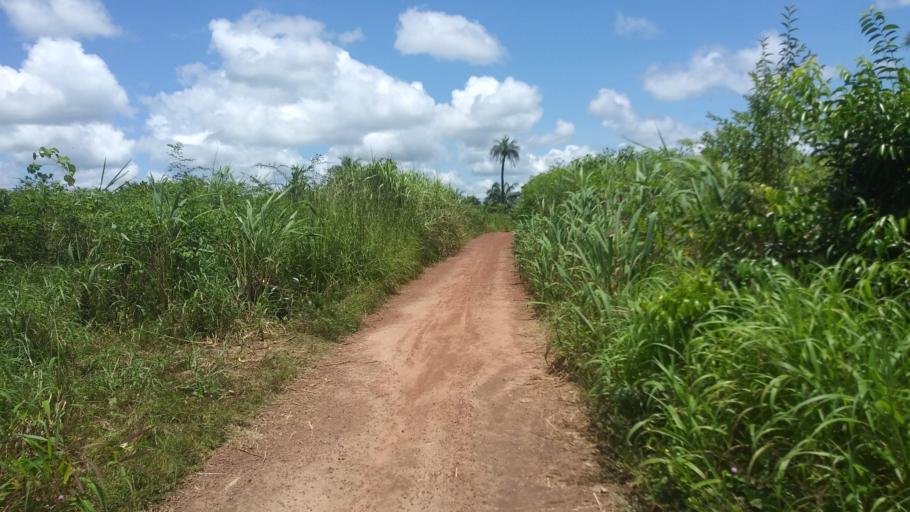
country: SL
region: Northern Province
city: Makeni
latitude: 8.8904
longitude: -12.0119
